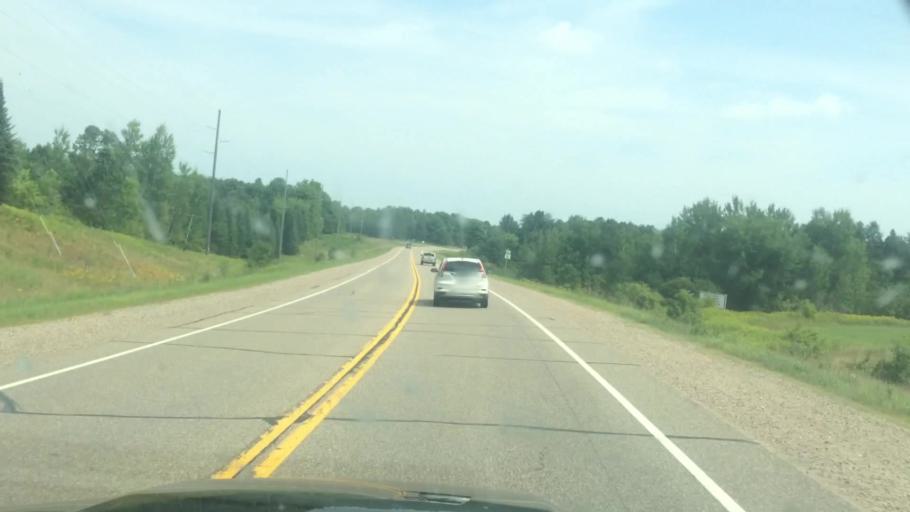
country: US
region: Wisconsin
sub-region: Langlade County
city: Antigo
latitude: 45.1635
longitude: -89.0139
